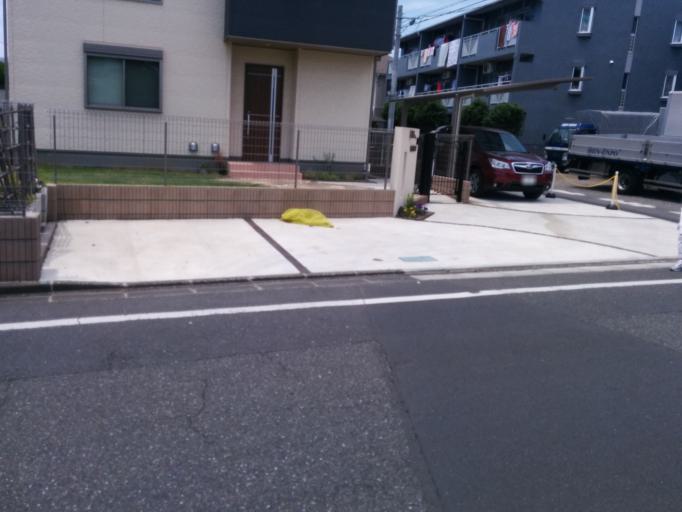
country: JP
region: Tokyo
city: Higashimurayama-shi
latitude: 35.7630
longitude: 139.4773
